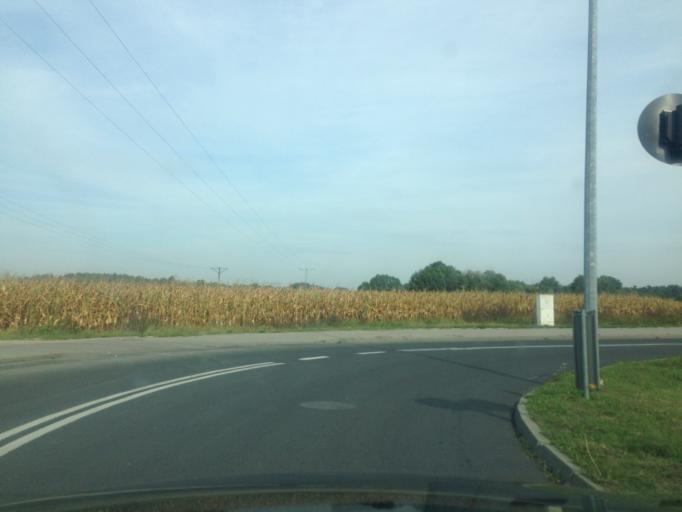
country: PL
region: Kujawsko-Pomorskie
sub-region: Powiat aleksandrowski
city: Ciechocinek
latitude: 52.8761
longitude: 18.7705
